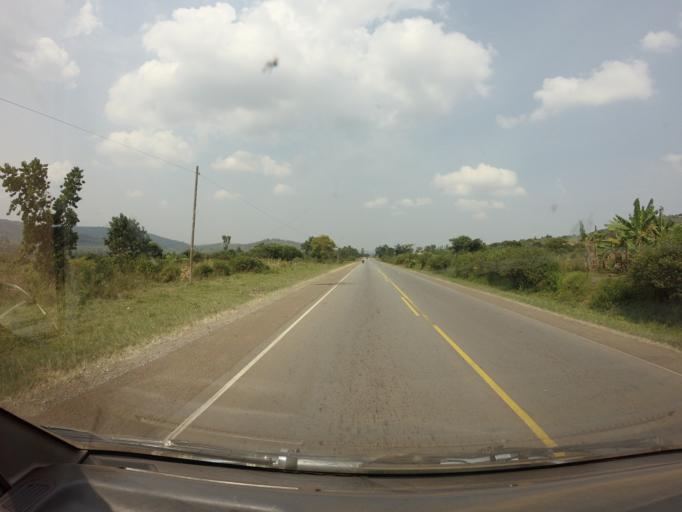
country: UG
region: Central Region
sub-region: Lwengo District
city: Lwengo
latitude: -0.3802
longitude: 31.2966
